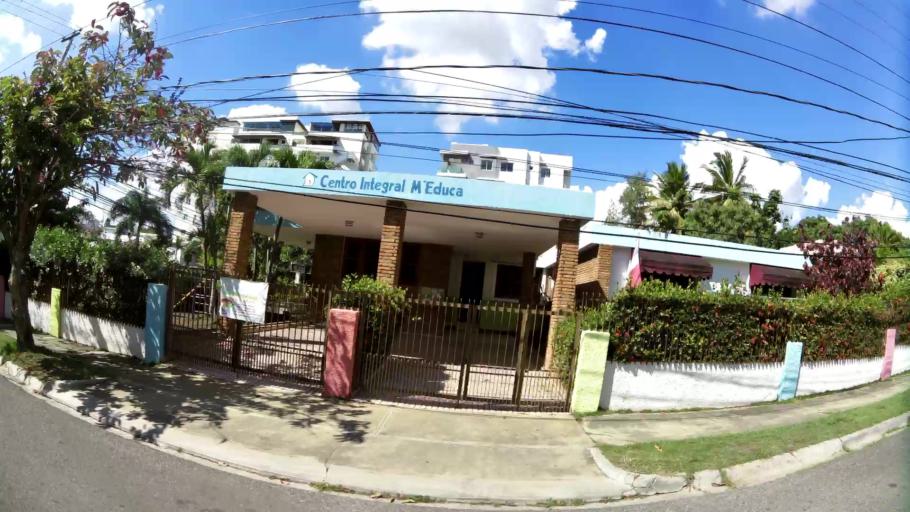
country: DO
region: Santiago
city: Santiago de los Caballeros
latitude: 19.4549
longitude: -70.6818
